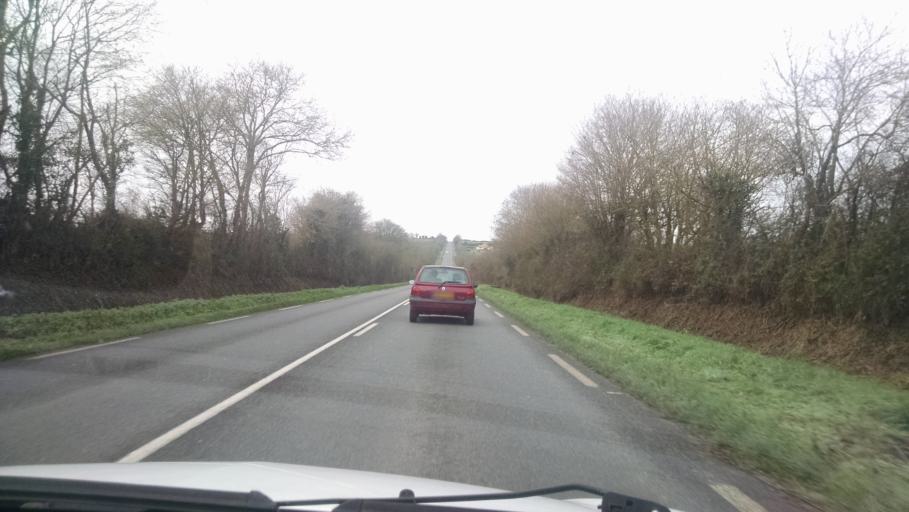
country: FR
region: Pays de la Loire
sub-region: Departement de Maine-et-Loire
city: La Seguiniere
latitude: 47.0589
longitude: -0.9507
